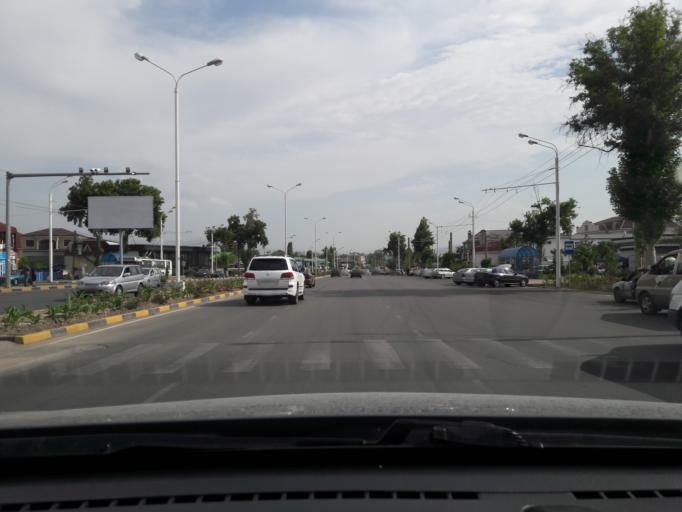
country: TJ
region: Dushanbe
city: Dushanbe
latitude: 38.5405
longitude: 68.7552
